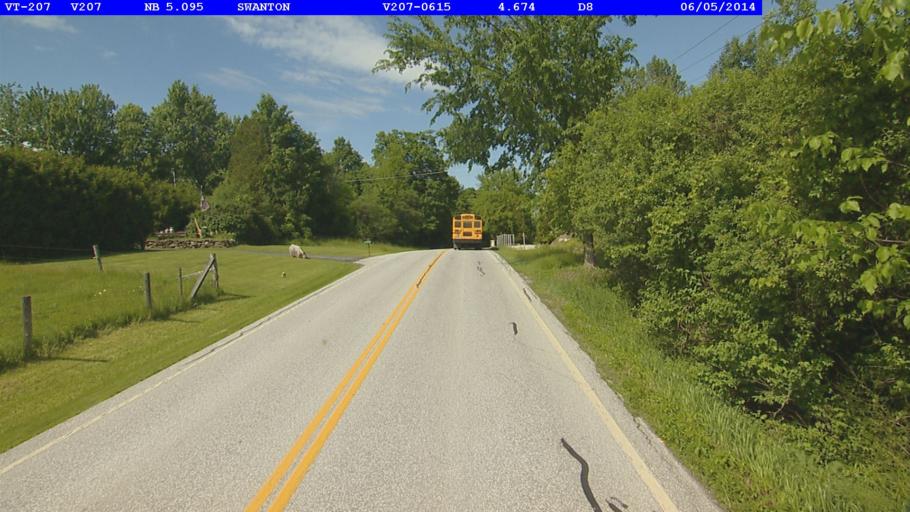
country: US
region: Vermont
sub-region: Franklin County
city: Swanton
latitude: 44.9106
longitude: -73.0603
